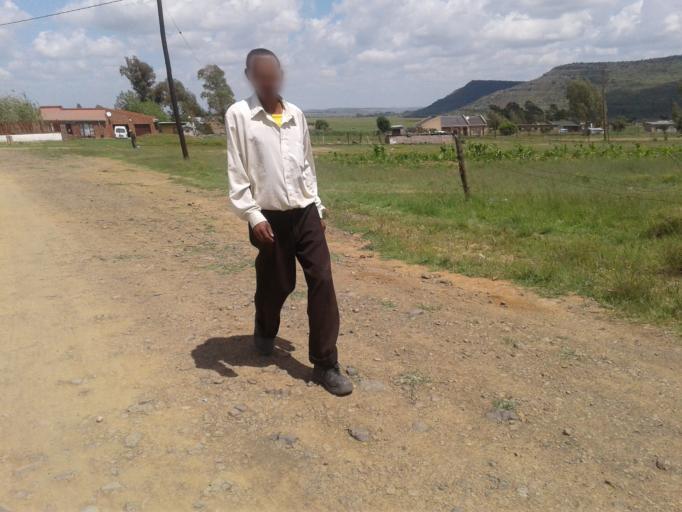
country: LS
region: Mafeteng
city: Mafeteng
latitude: -29.7533
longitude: 27.1121
